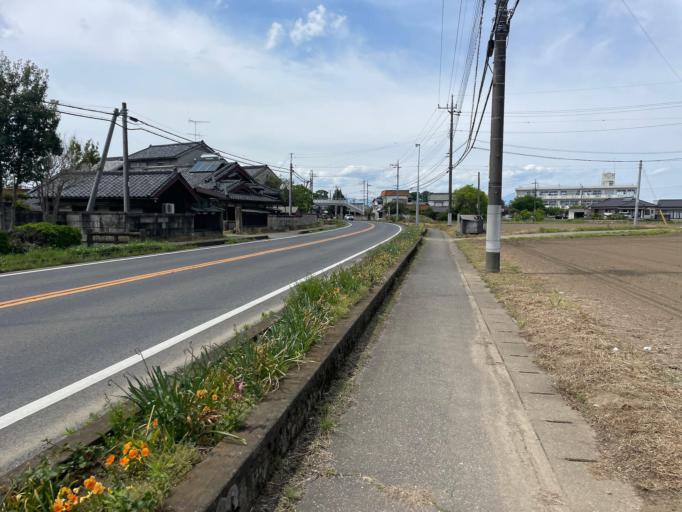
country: JP
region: Tochigi
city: Mibu
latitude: 36.4487
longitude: 139.7791
